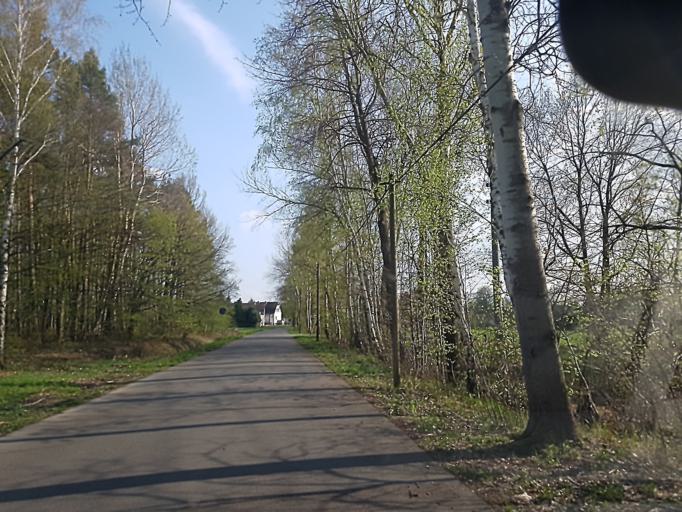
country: DE
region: Brandenburg
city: Trobitz
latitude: 51.5772
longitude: 13.4127
